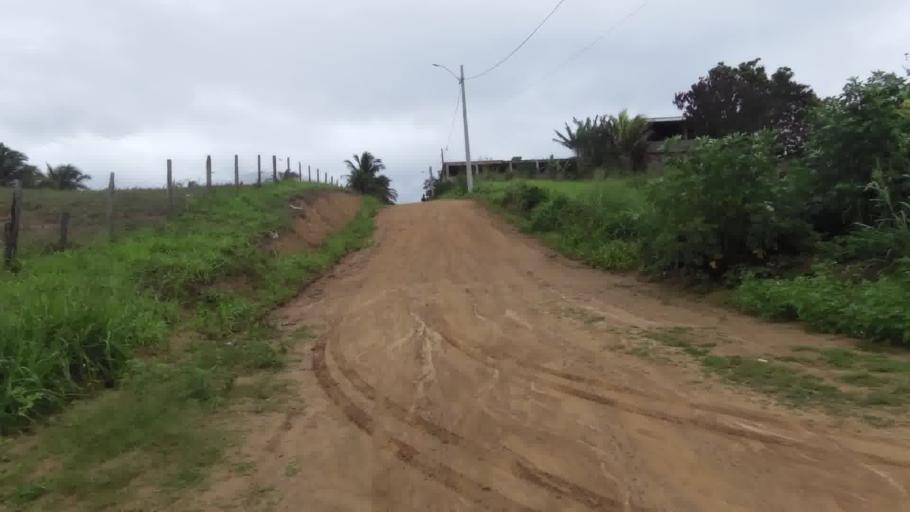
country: BR
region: Espirito Santo
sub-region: Marataizes
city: Marataizes
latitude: -21.0500
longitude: -40.8369
